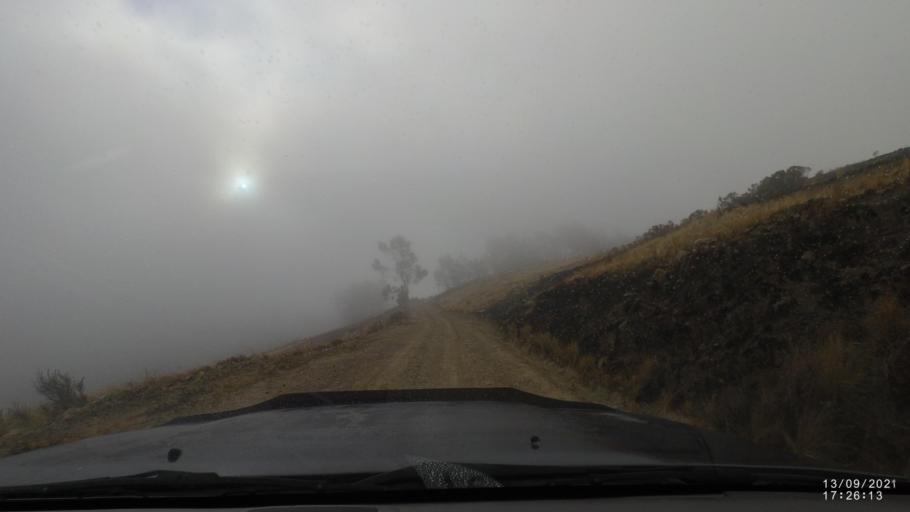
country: BO
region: Cochabamba
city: Colomi
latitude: -17.3609
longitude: -65.7840
